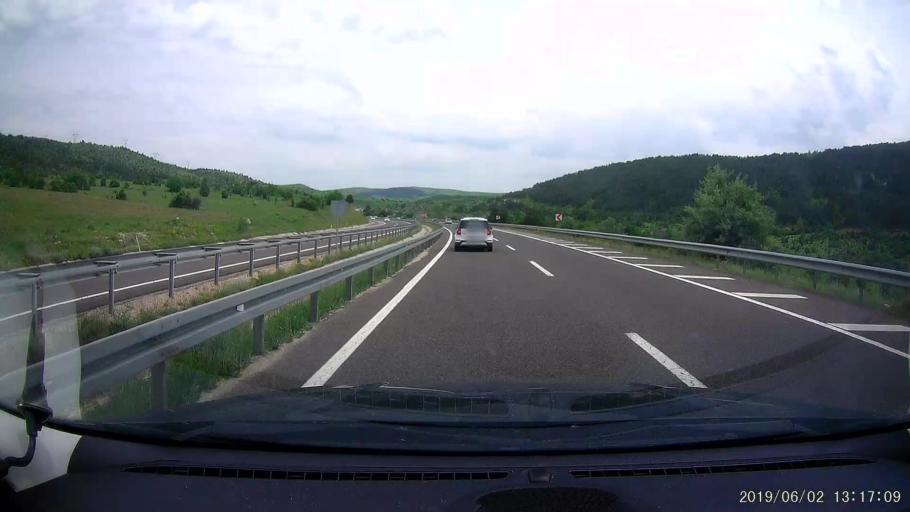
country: TR
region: Karabuk
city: Gozyeri
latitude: 40.8417
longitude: 32.6963
